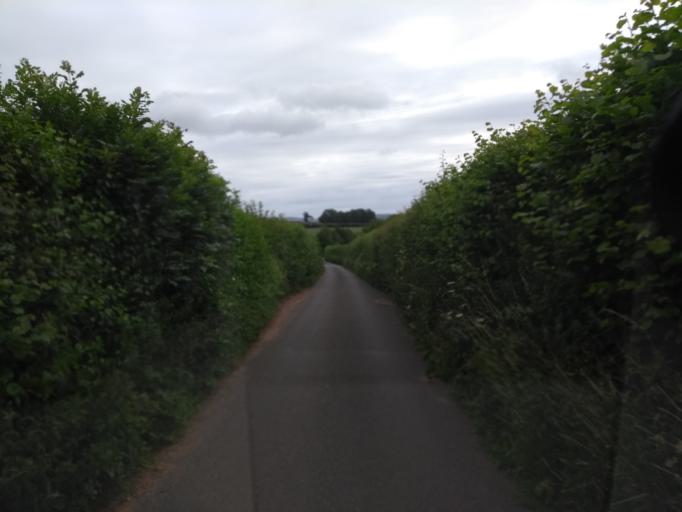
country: GB
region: England
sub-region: Somerset
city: Bishops Lydeard
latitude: 51.0379
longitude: -3.2433
